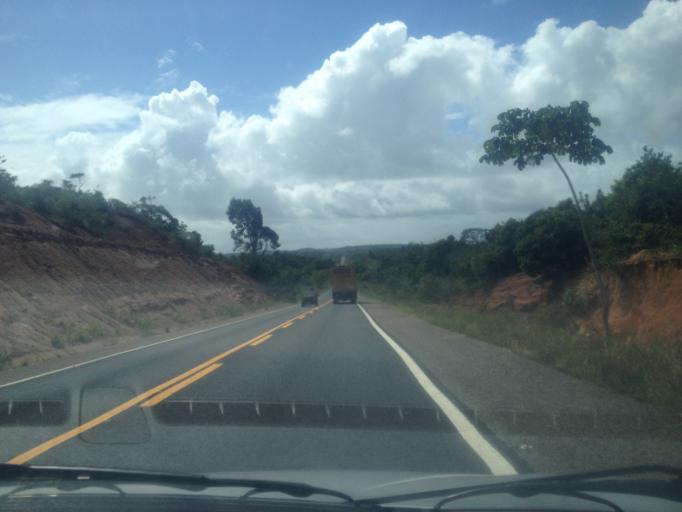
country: BR
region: Sergipe
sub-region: Indiaroba
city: Indiaroba
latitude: -11.6406
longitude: -37.5410
